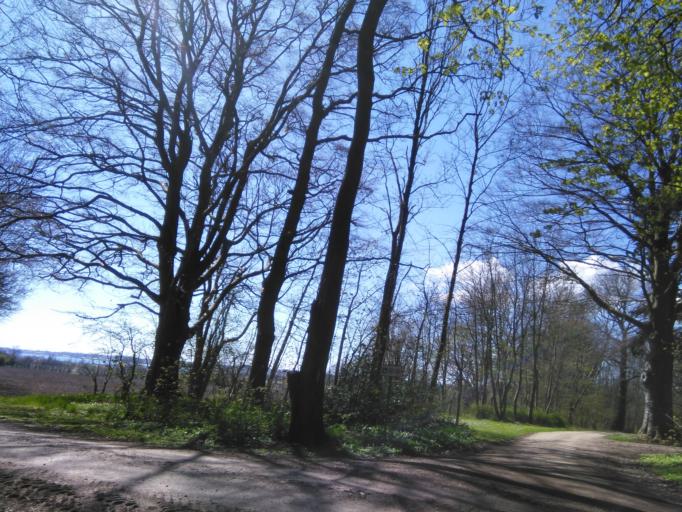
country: DK
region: Central Jutland
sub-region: Hedensted Kommune
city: Juelsminde
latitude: 55.7462
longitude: 10.0300
